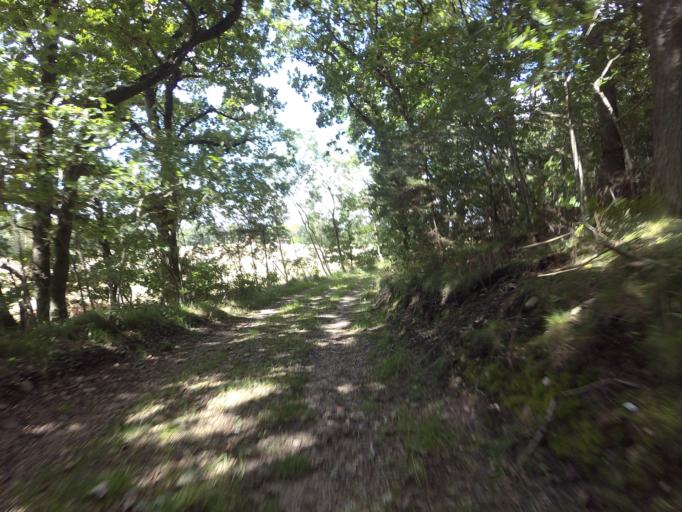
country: DK
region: Central Jutland
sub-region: Silkeborg Kommune
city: Svejbaek
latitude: 56.2167
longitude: 9.6892
